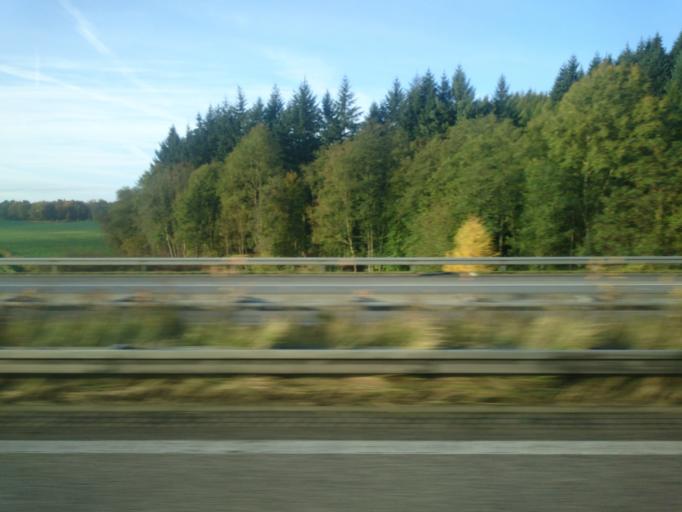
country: DE
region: Mecklenburg-Vorpommern
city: Lalendorf
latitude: 53.7283
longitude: 12.3528
